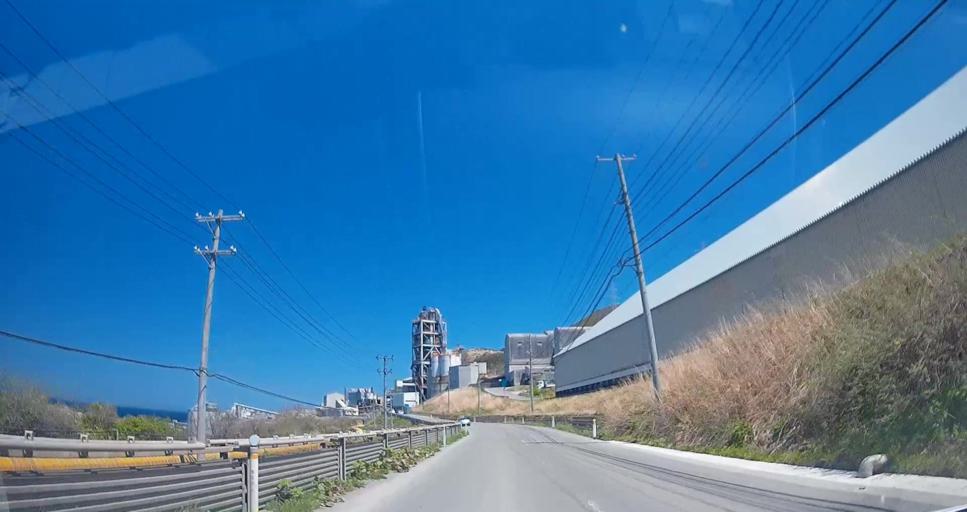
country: JP
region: Aomori
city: Mutsu
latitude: 41.4043
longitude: 141.4321
